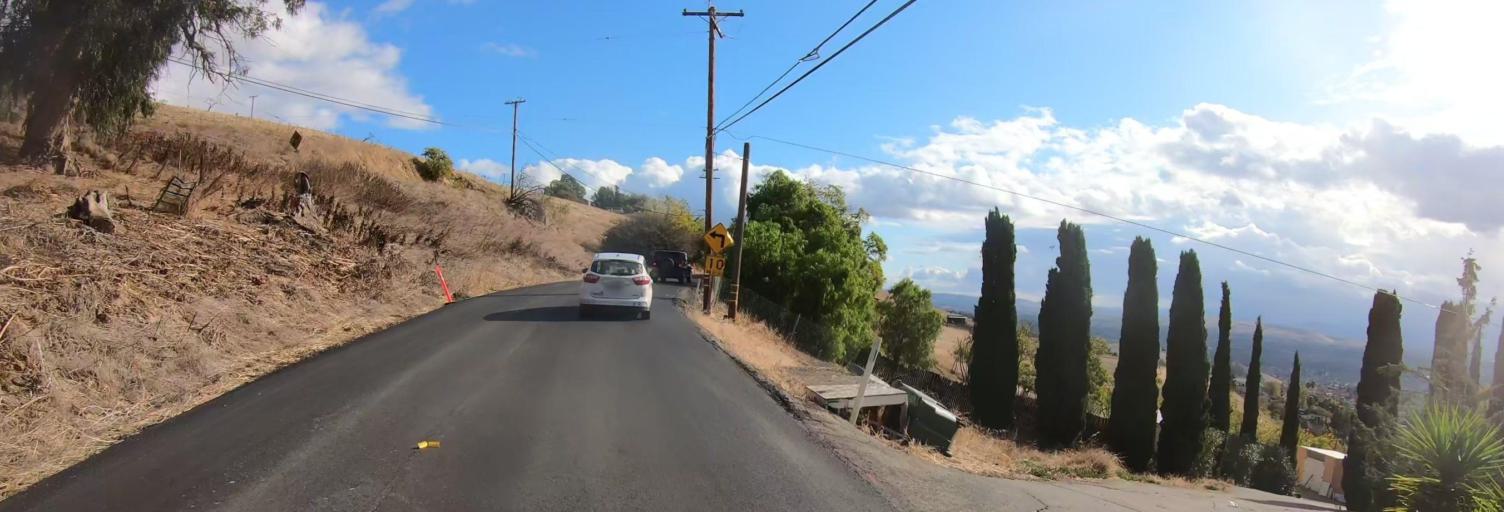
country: US
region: California
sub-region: Santa Clara County
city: East Foothills
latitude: 37.3750
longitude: -121.7993
